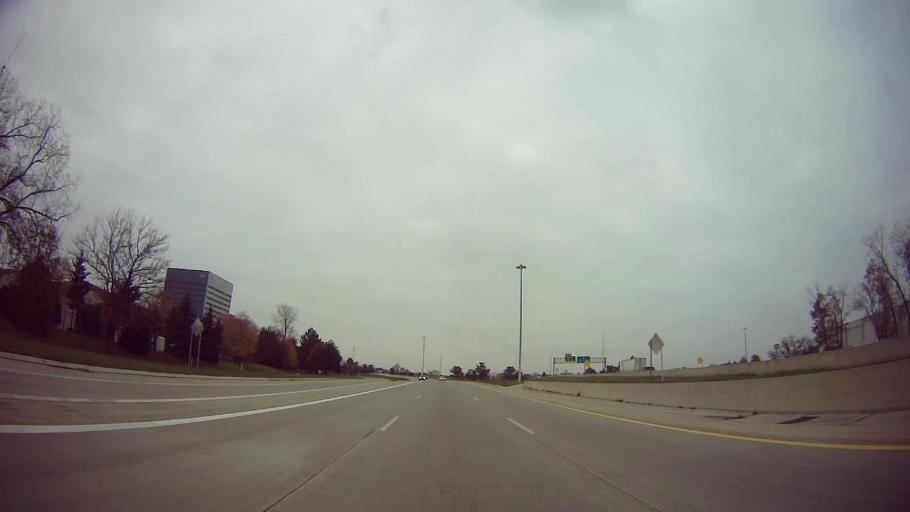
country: US
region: Michigan
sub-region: Oakland County
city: Southfield
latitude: 42.4620
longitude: -83.2205
